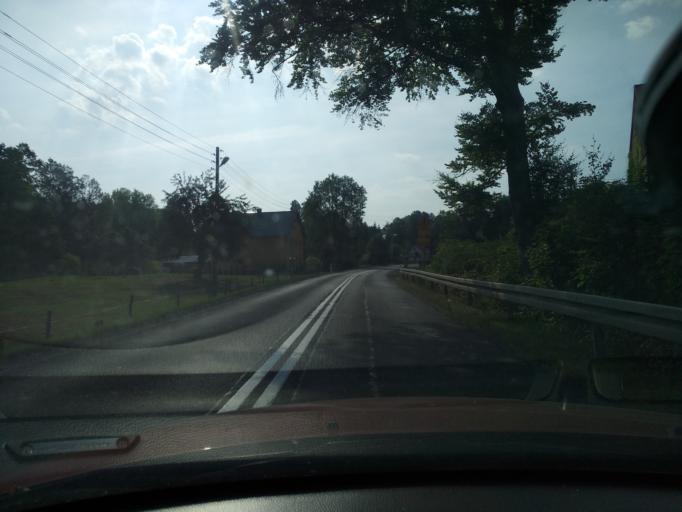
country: PL
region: Lower Silesian Voivodeship
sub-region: Powiat lwowecki
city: Lubomierz
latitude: 50.9715
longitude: 15.5041
